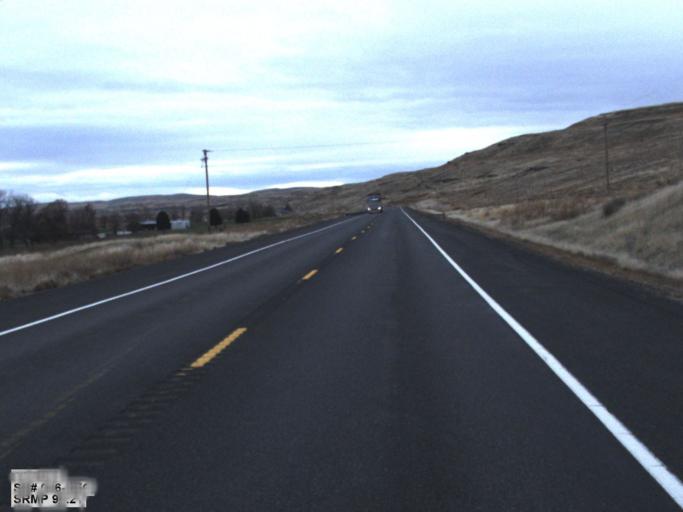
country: US
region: Washington
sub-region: Columbia County
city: Dayton
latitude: 46.7763
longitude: -118.0554
